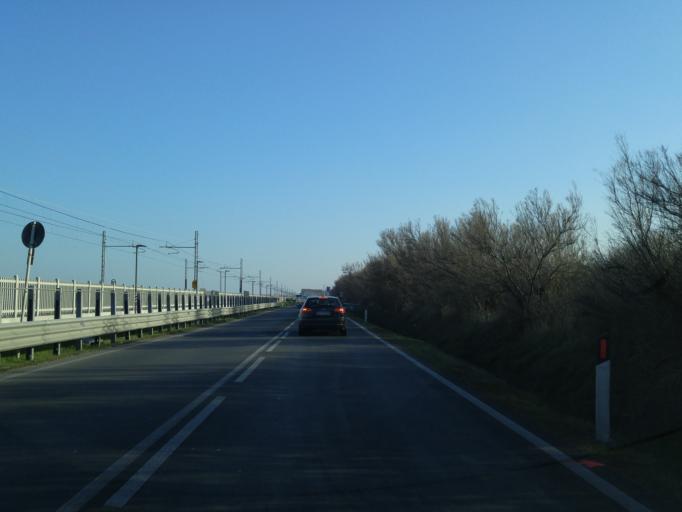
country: IT
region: The Marches
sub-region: Provincia di Pesaro e Urbino
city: Fenile
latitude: 43.8647
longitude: 12.9863
